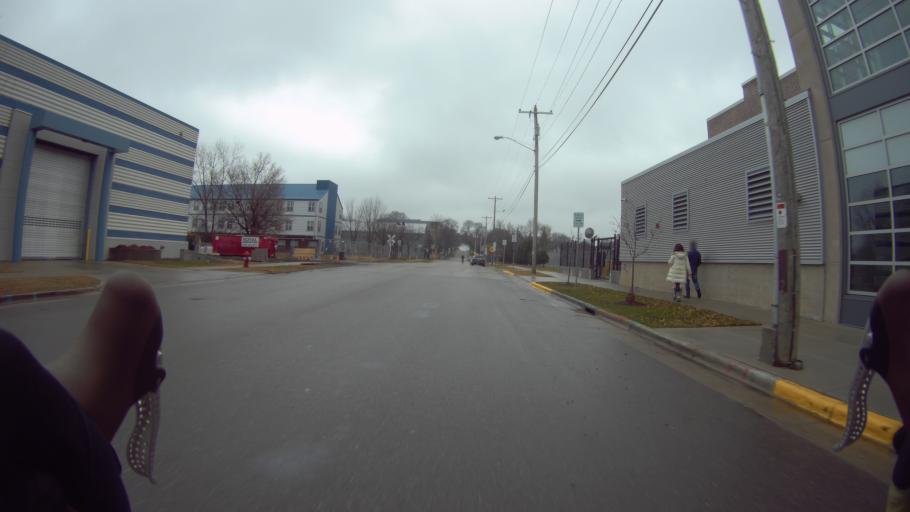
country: US
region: Wisconsin
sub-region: Dane County
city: Madison
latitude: 43.0811
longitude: -89.3716
